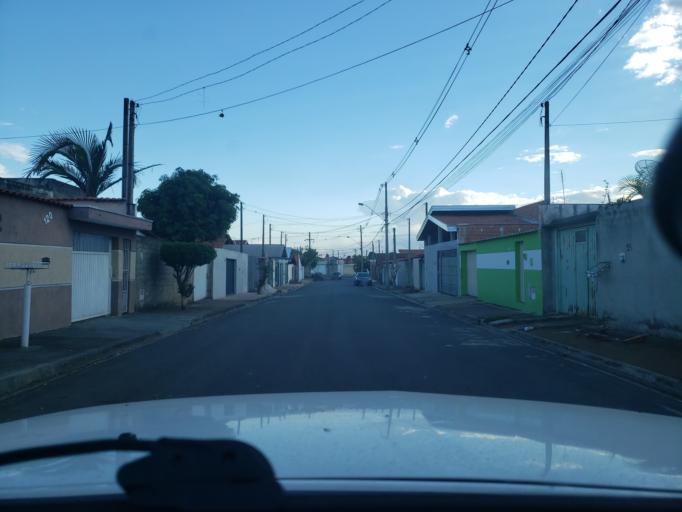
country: BR
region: Sao Paulo
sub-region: Moji-Guacu
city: Mogi-Gaucu
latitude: -22.3293
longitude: -46.9247
